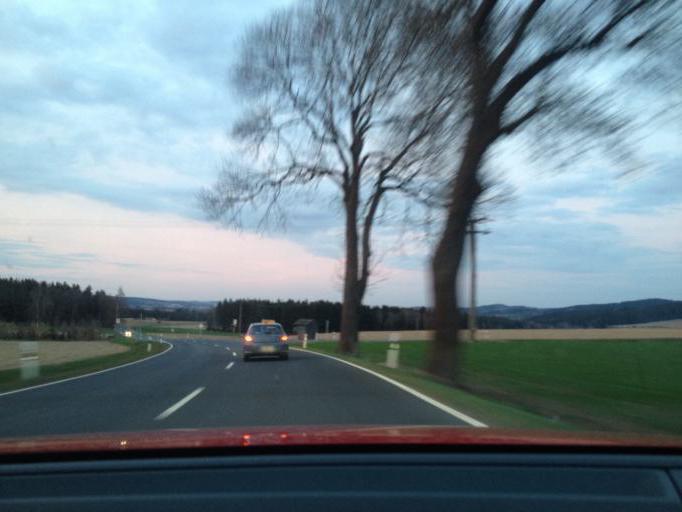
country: DE
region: Bavaria
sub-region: Upper Palatinate
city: Pullenreuth
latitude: 49.9518
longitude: 12.0274
